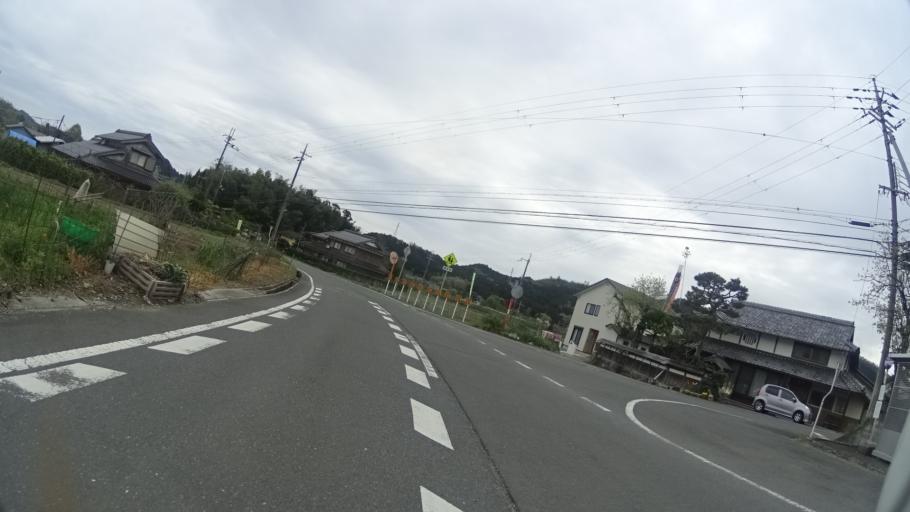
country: JP
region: Kyoto
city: Ayabe
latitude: 35.2018
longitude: 135.4603
